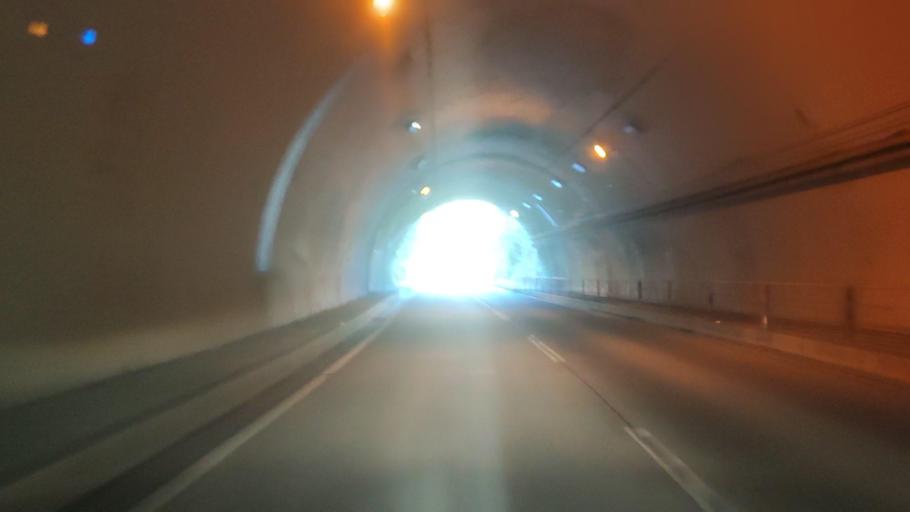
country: JP
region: Miyazaki
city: Nobeoka
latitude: 32.6941
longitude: 131.8118
